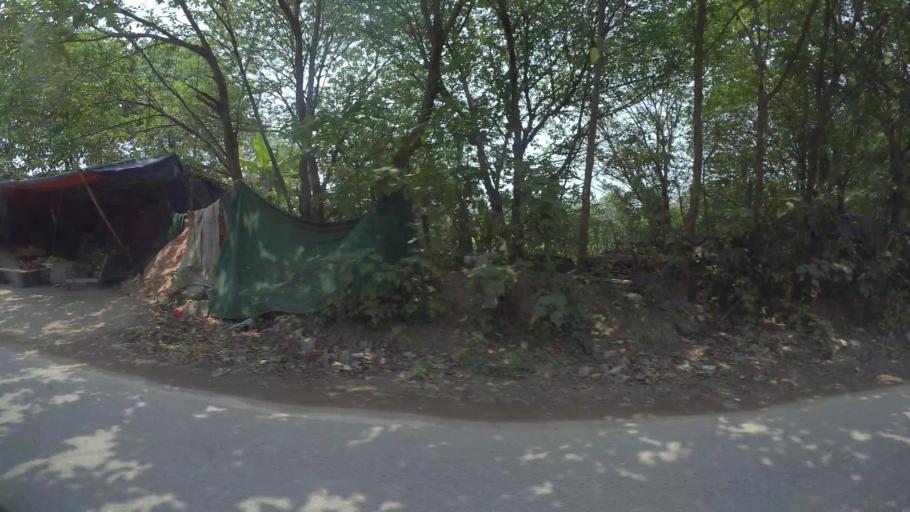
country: VN
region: Ha Noi
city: Thanh Xuan
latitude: 21.0041
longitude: 105.7683
